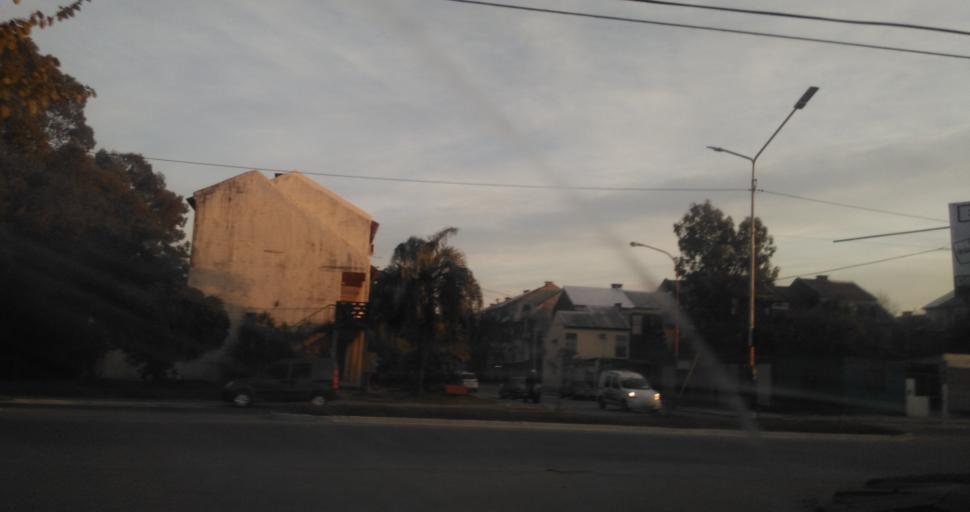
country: AR
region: Chaco
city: Resistencia
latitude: -27.4623
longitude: -59.0127
